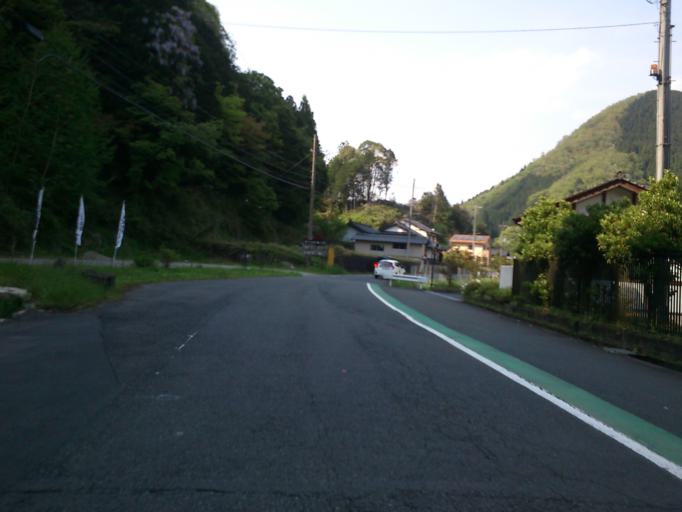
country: JP
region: Kyoto
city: Fukuchiyama
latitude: 35.3270
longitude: 135.0054
